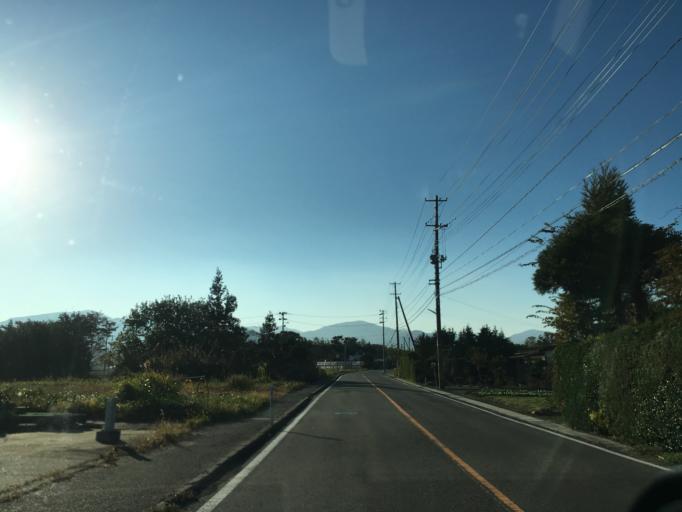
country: JP
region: Fukushima
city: Koriyama
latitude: 37.3928
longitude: 140.2812
